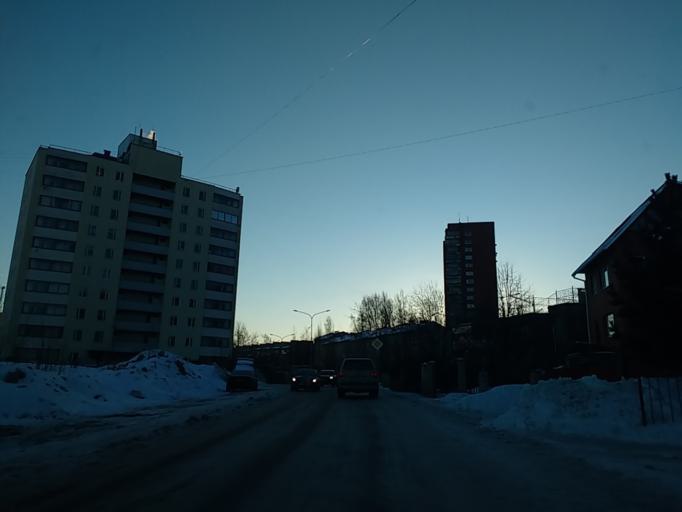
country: RU
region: Republic of Karelia
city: Petrozavodsk
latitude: 61.7747
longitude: 34.3868
